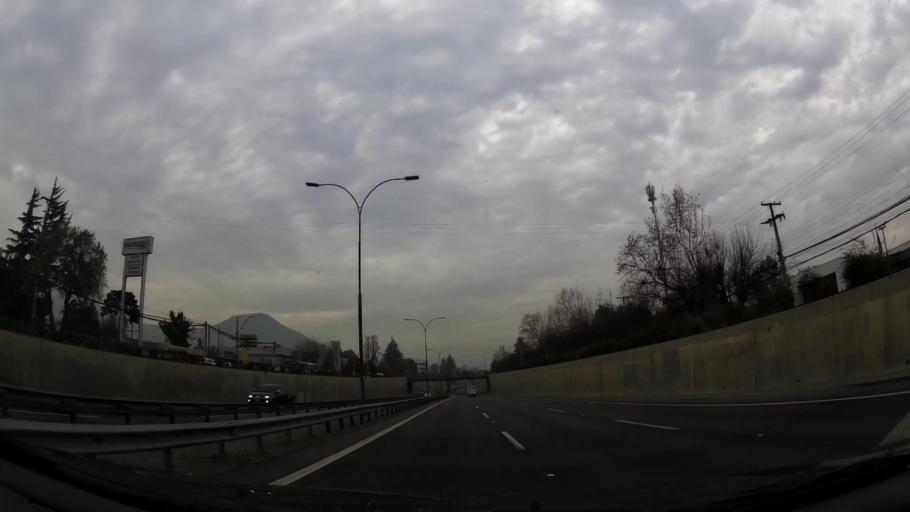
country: CL
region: Santiago Metropolitan
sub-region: Provincia de Santiago
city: Lo Prado
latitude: -33.3927
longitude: -70.6878
